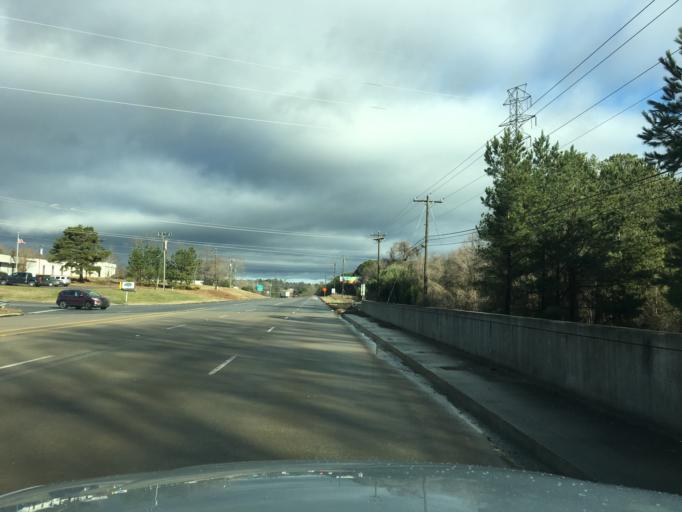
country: US
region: South Carolina
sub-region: Spartanburg County
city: Mayo
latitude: 35.0190
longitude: -81.8729
